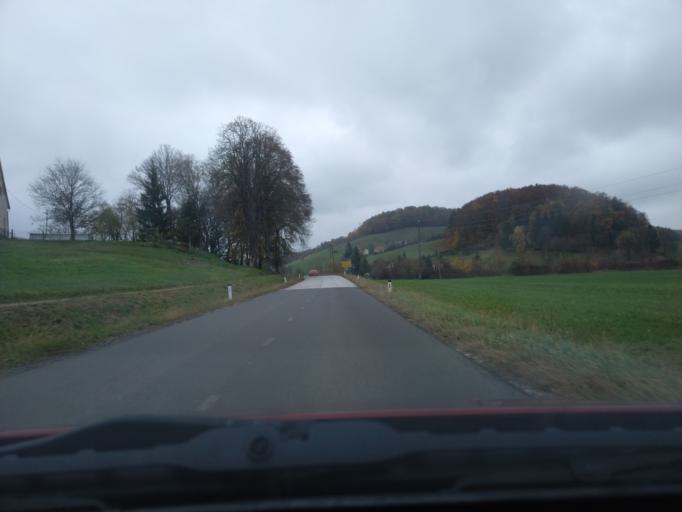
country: SI
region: Kungota
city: Zgornja Kungota
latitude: 46.6457
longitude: 15.6135
